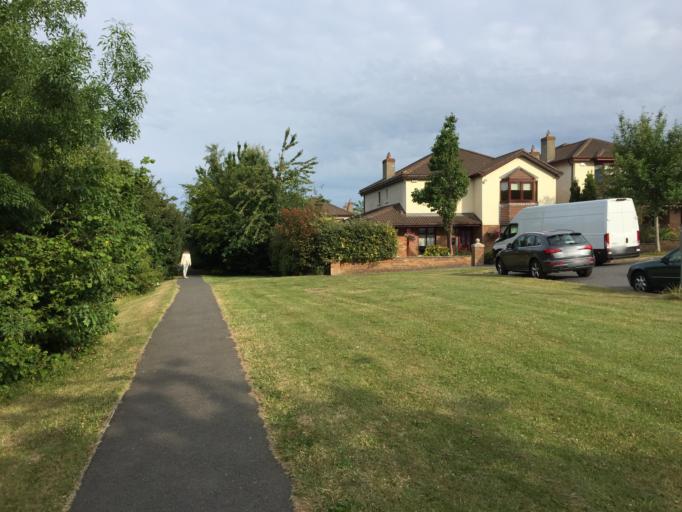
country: IE
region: Leinster
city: Loughlinstown
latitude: 53.2473
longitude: -6.1424
